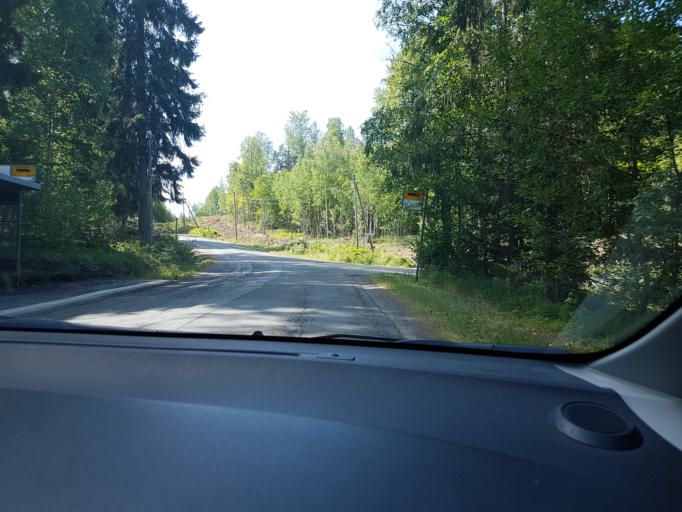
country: FI
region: Uusimaa
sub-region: Helsinki
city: Kilo
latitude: 60.3306
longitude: 24.7713
